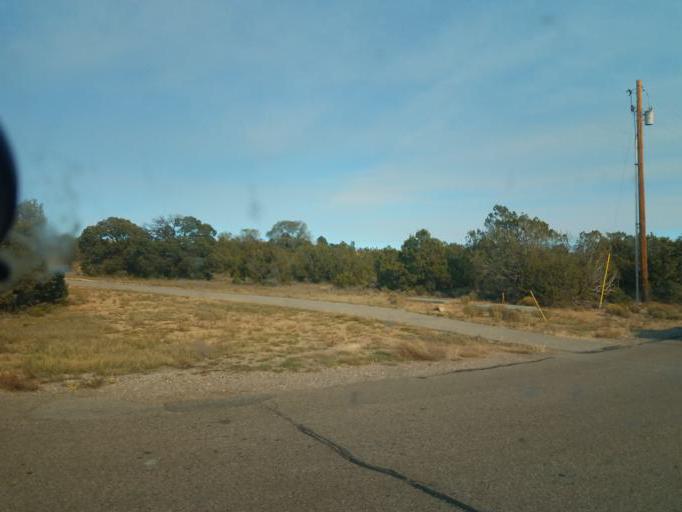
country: US
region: New Mexico
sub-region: Los Alamos County
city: White Rock
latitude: 35.8134
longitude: -106.2233
